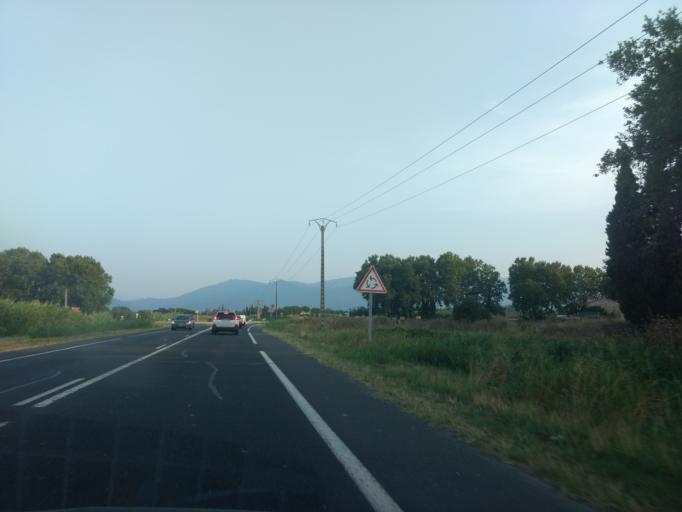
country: FR
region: Languedoc-Roussillon
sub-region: Departement des Pyrenees-Orientales
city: Latour-Bas-Elne
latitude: 42.5975
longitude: 3.0247
